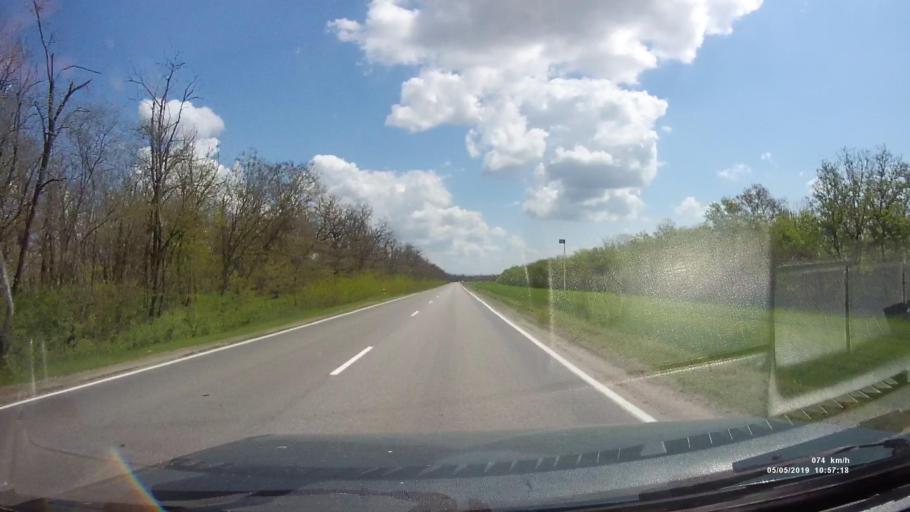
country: RU
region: Rostov
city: Ust'-Donetskiy
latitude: 47.6711
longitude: 40.8339
